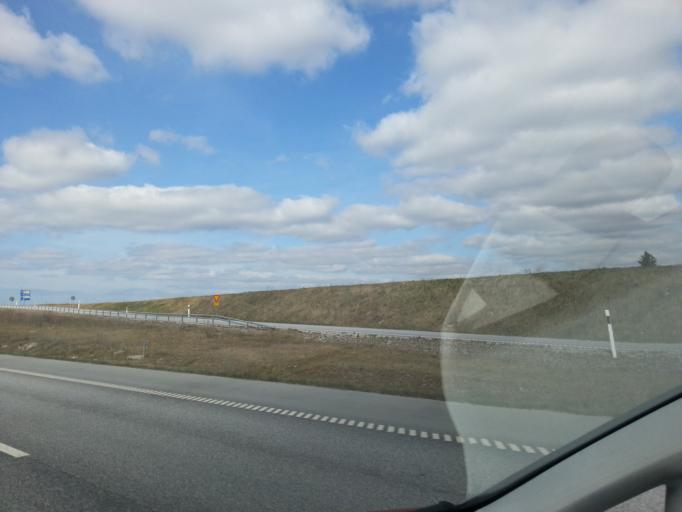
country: SE
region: Skane
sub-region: Vellinge Kommun
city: Vellinge
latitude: 55.4527
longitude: 13.0215
